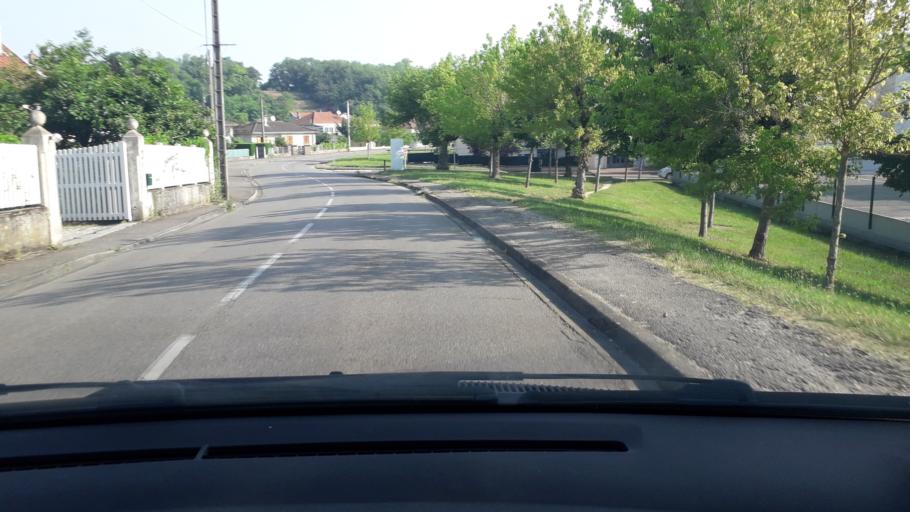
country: FR
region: Rhone-Alpes
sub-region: Departement de l'Isere
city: Pont-de-Cheruy
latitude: 45.7610
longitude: 5.1782
